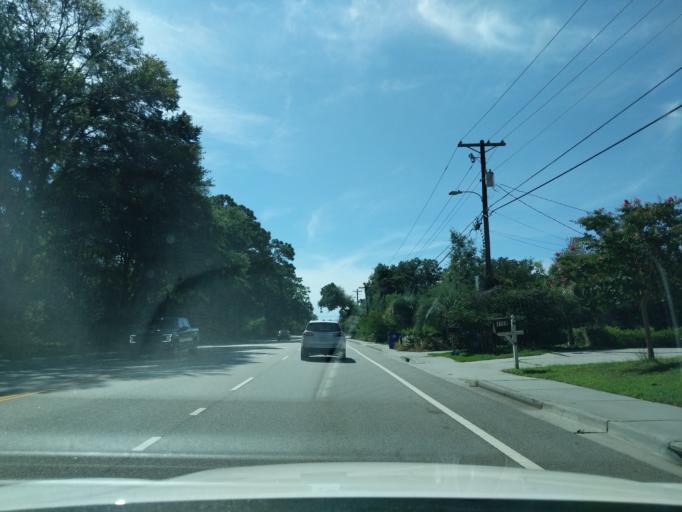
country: US
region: South Carolina
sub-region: Charleston County
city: Charleston
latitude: 32.7472
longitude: -79.9429
